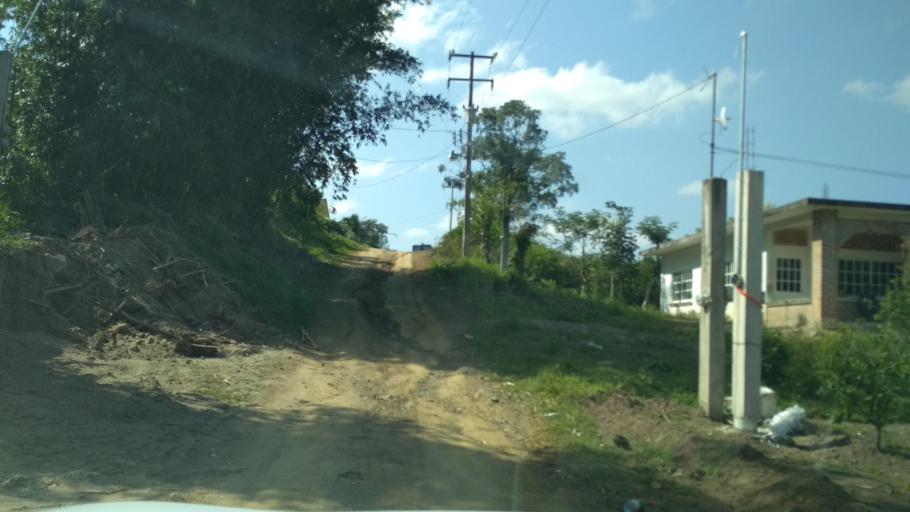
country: MX
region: Puebla
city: San Jose Acateno
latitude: 20.1899
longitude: -97.1543
